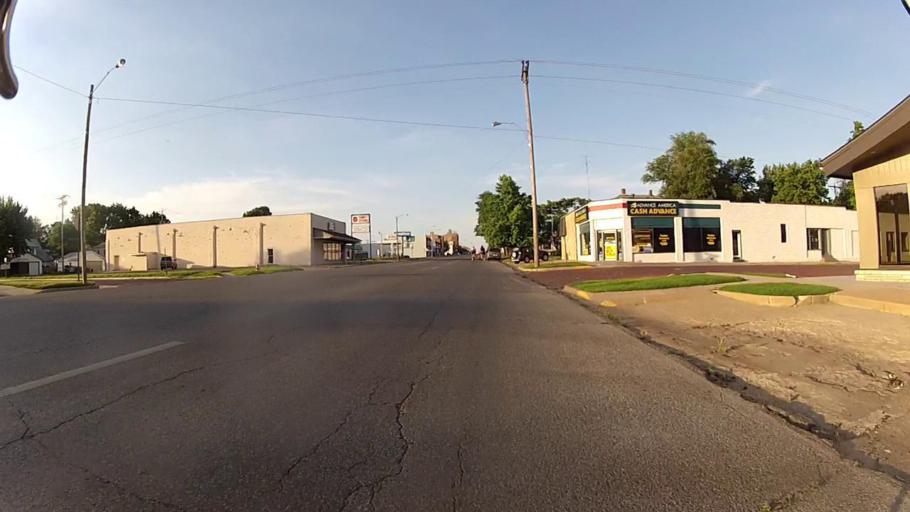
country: US
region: Kansas
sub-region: Cowley County
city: Arkansas City
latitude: 37.0660
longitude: -97.0392
